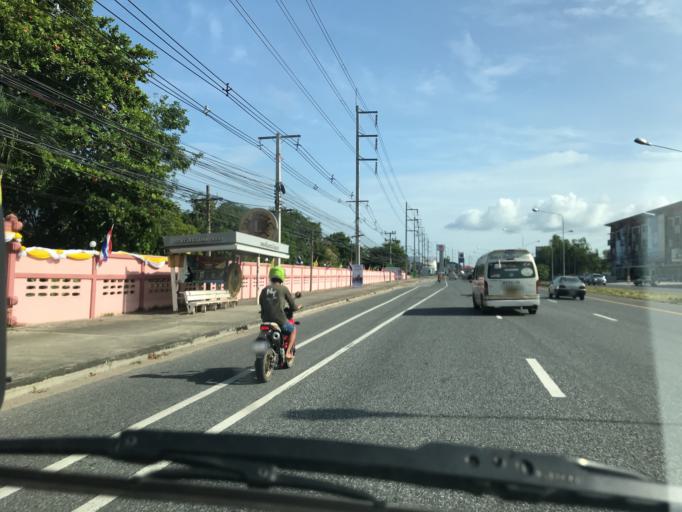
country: TH
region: Chon Buri
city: Bang Lamung
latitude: 13.0347
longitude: 100.9281
